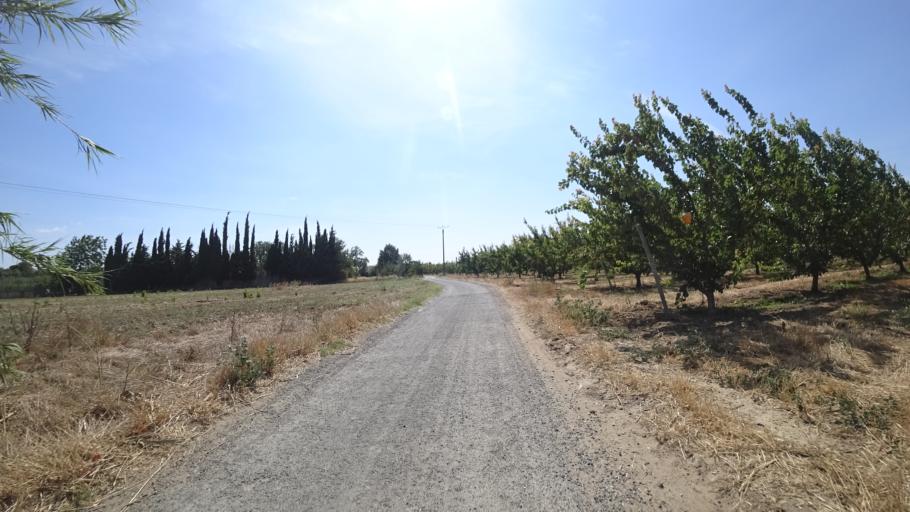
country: FR
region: Languedoc-Roussillon
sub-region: Departement des Pyrenees-Orientales
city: Rivesaltes
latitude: 42.7753
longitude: 2.8898
